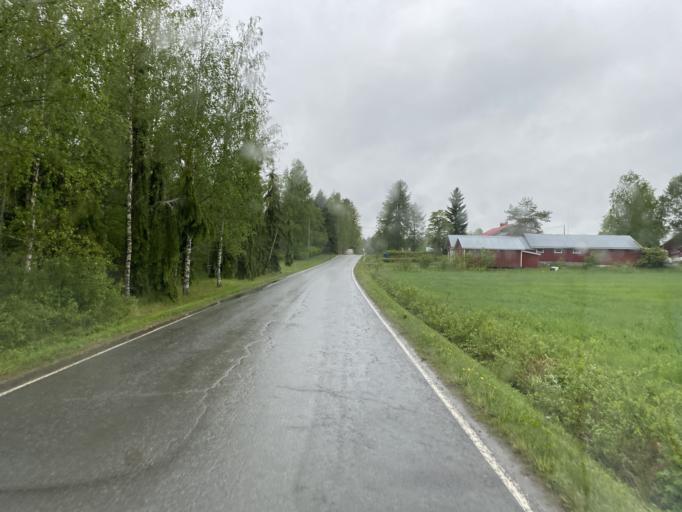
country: FI
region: Pirkanmaa
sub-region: Etelae-Pirkanmaa
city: Urjala
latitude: 60.9642
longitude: 23.5147
